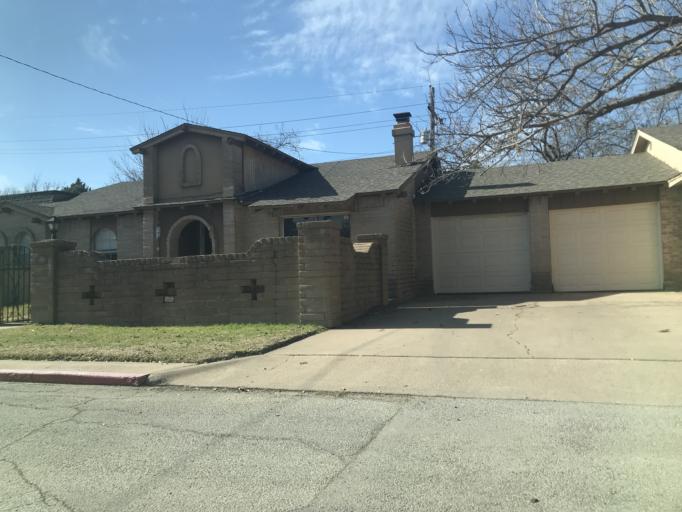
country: US
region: Texas
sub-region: Taylor County
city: Abilene
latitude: 32.4186
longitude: -99.7576
